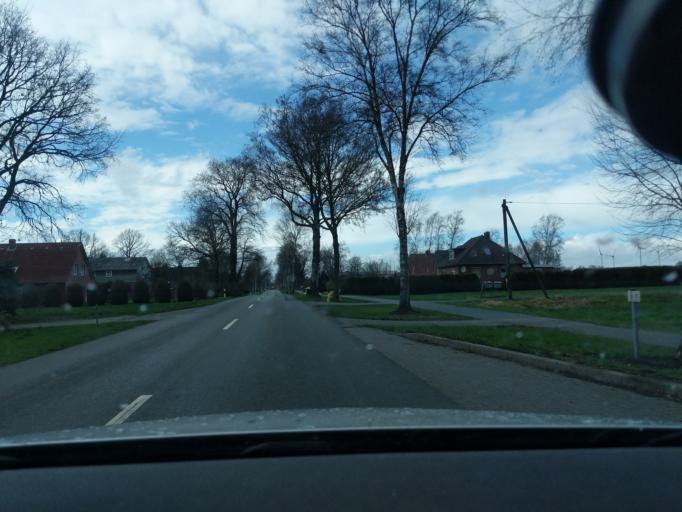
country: DE
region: Lower Saxony
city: Drochtersen
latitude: 53.6662
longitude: 9.3919
